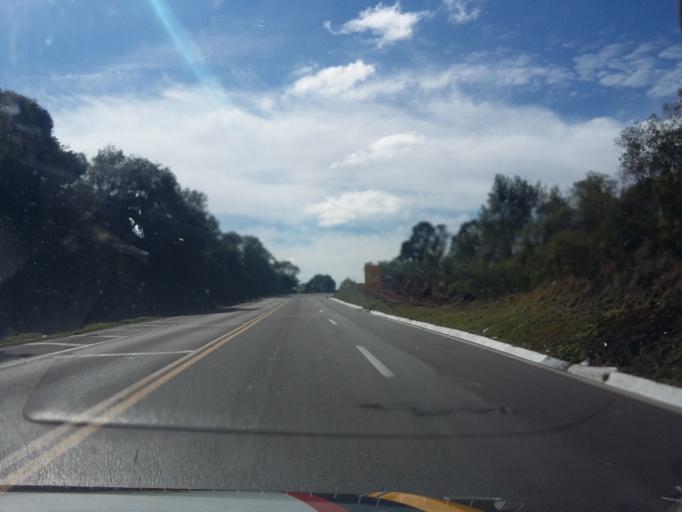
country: BR
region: Rio Grande do Sul
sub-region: Vacaria
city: Vacaria
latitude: -28.5799
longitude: -51.0233
